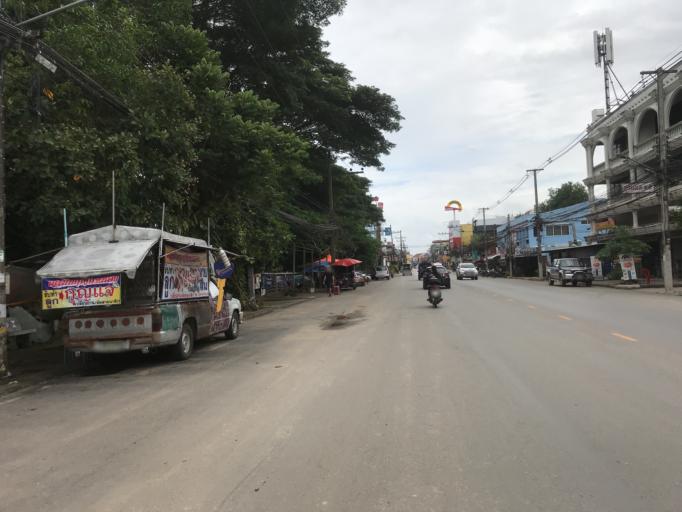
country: TH
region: Chiang Rai
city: Chiang Rai
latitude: 19.8937
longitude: 99.8312
